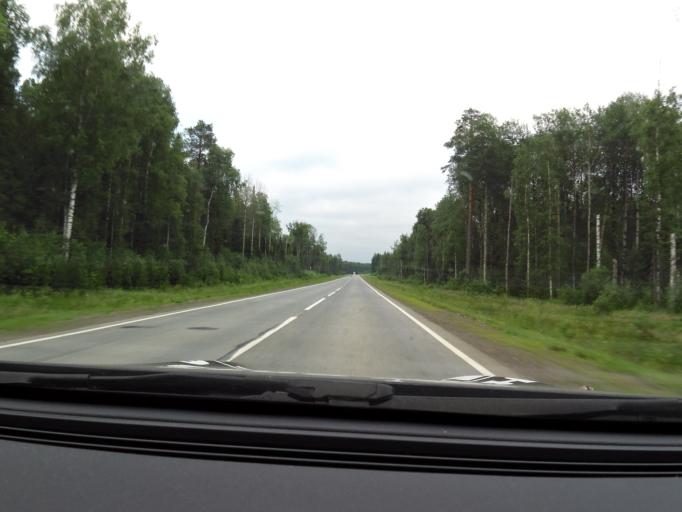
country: RU
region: Perm
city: Zyukayka
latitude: 58.3701
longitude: 54.6588
